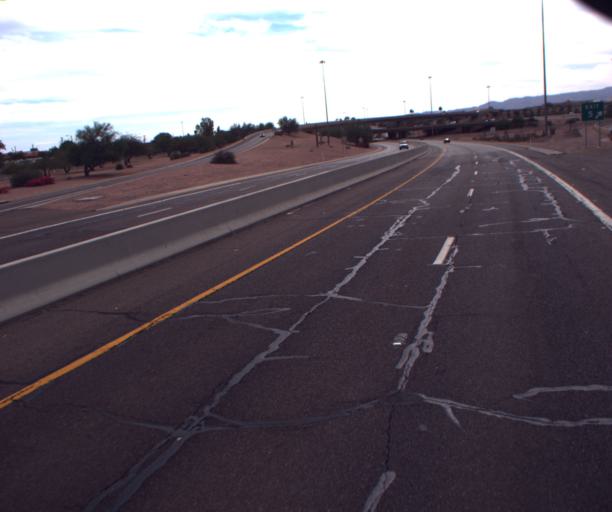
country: US
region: Arizona
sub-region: Maricopa County
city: Tempe Junction
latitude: 33.4620
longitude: -111.9831
